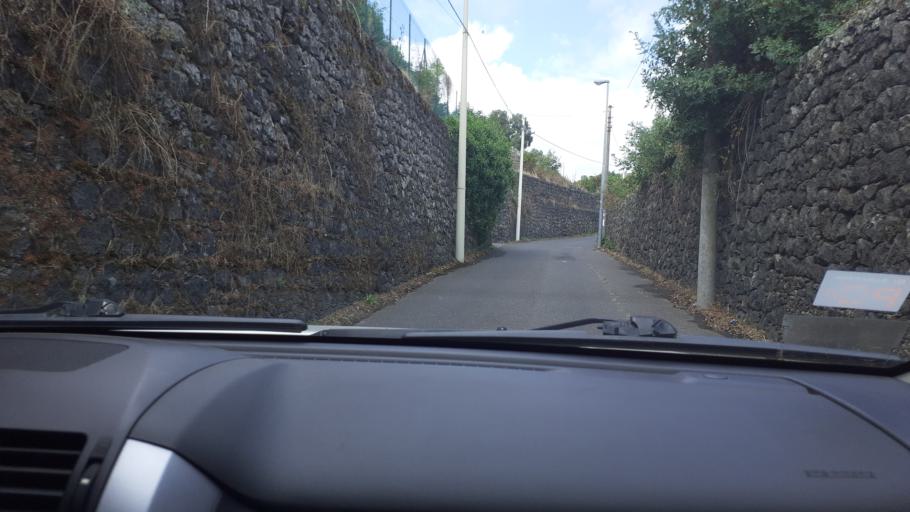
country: IT
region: Sicily
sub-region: Catania
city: San Giovanni la Punta
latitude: 37.5919
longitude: 15.0828
